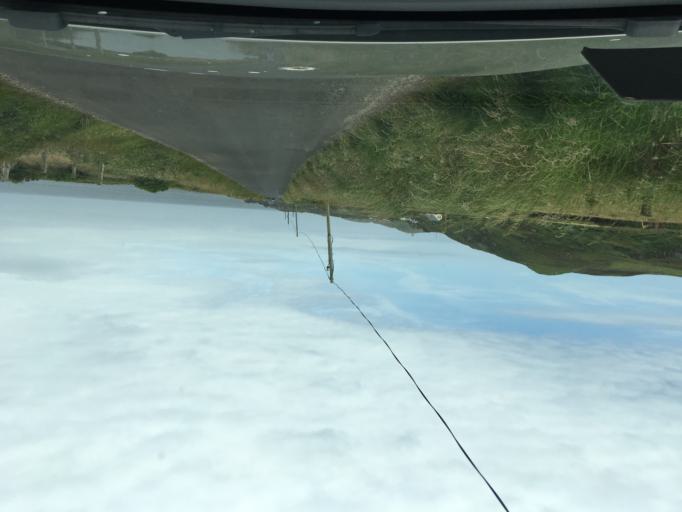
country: IE
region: Ulster
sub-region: County Donegal
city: Carndonagh
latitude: 55.3727
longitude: -7.3419
